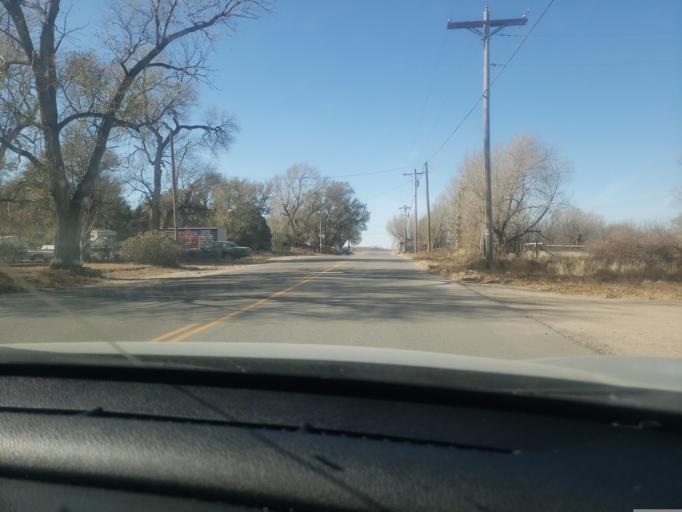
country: US
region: Kansas
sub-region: Finney County
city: Garden City
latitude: 37.9515
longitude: -100.8757
